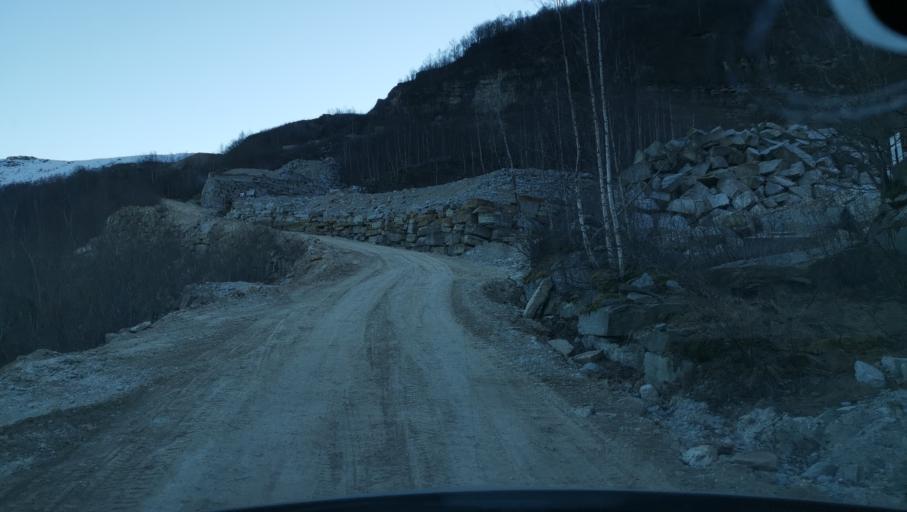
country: IT
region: Piedmont
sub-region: Provincia di Torino
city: Rora
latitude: 44.7573
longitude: 7.1974
